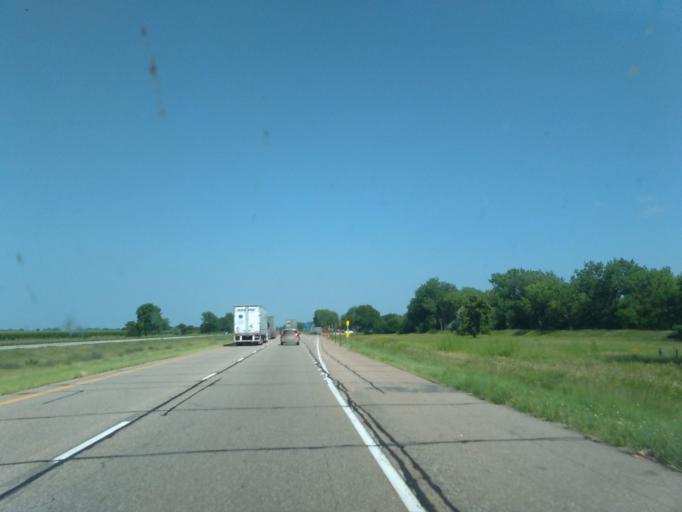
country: US
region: Nebraska
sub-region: Buffalo County
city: Kearney
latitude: 40.6713
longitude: -99.1627
